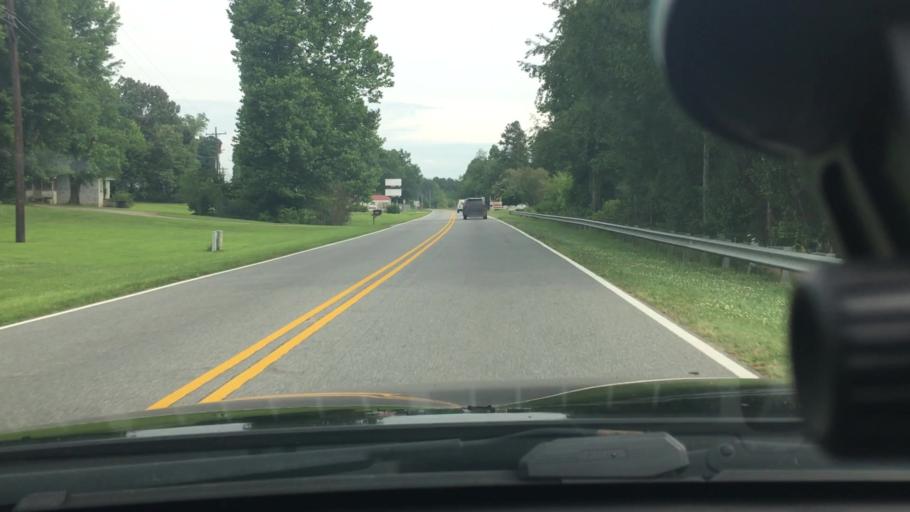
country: US
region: North Carolina
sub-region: Rutherford County
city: Rutherfordton
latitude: 35.4366
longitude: -81.9824
